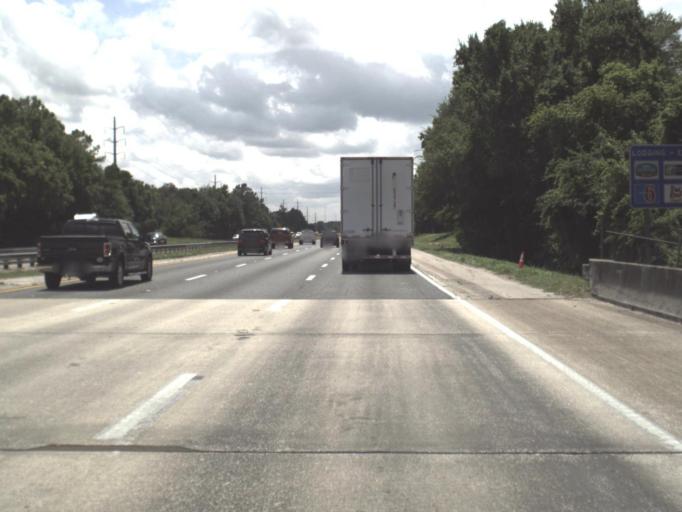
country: US
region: Florida
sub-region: Alachua County
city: Gainesville
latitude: 29.6320
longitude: -82.3967
